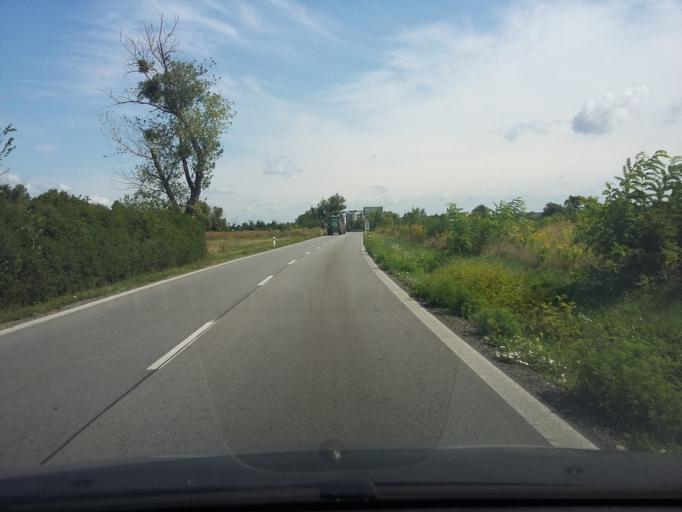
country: SK
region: Bratislavsky
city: Svaty Jur
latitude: 48.2401
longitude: 17.2552
